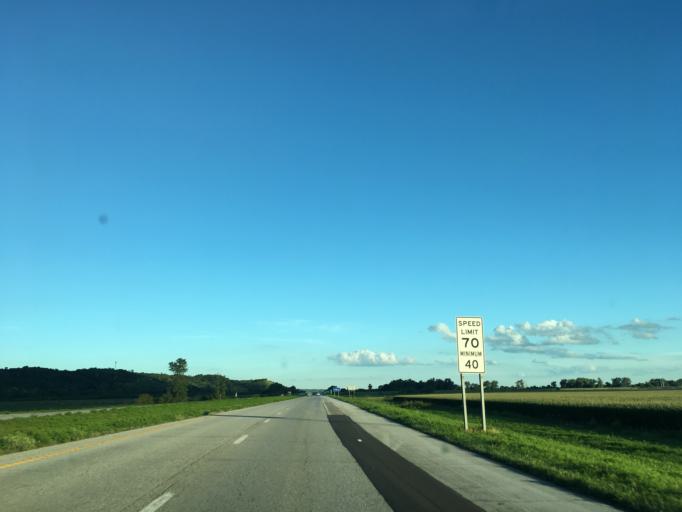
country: US
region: Iowa
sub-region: Fremont County
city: Hamburg
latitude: 40.5826
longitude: -95.6508
